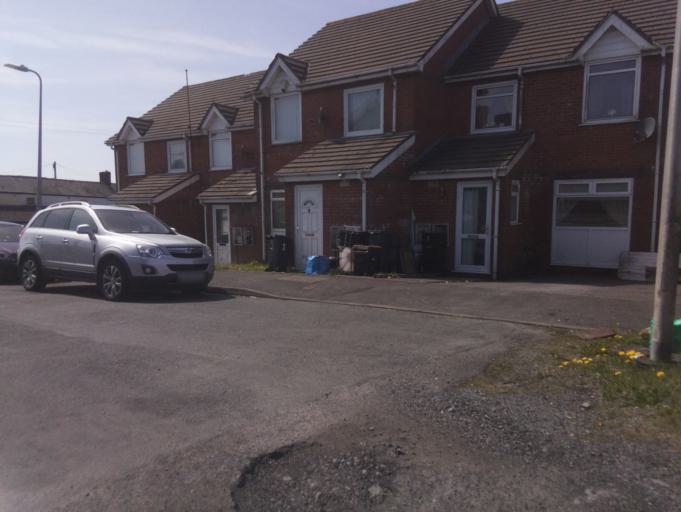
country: GB
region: Wales
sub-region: Merthyr Tydfil County Borough
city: Merthyr Tydfil
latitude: 51.7675
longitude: -3.3547
